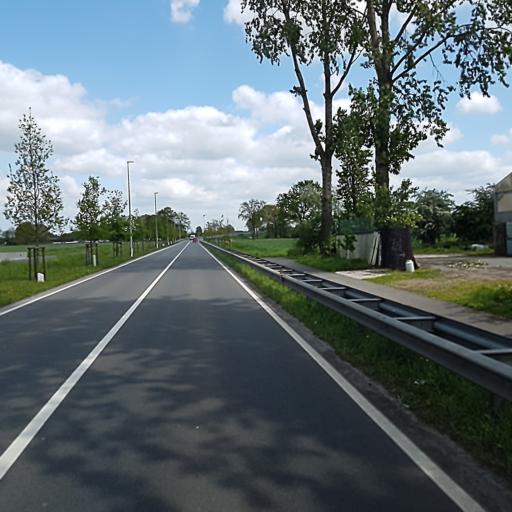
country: BE
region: Flanders
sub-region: Provincie Antwerpen
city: Brecht
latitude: 51.3580
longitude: 4.6273
